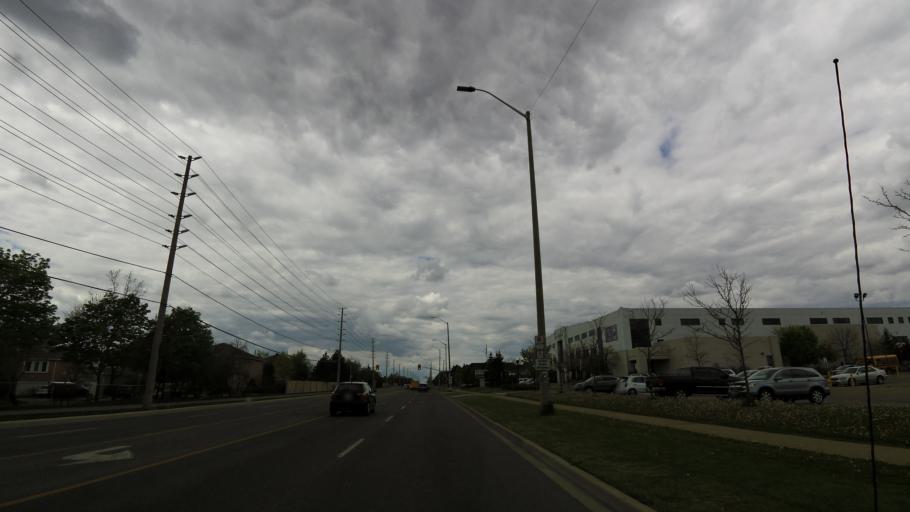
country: CA
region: Ontario
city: Mississauga
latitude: 43.5887
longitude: -79.6996
